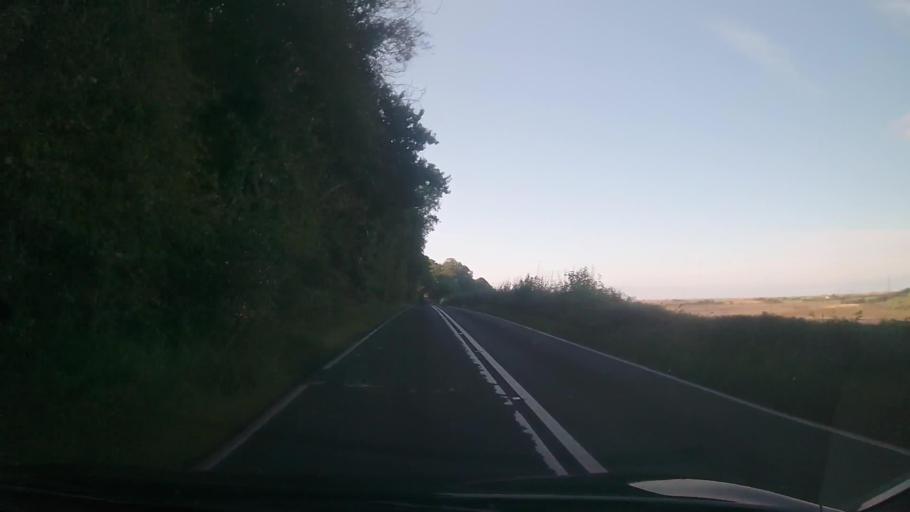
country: GB
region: England
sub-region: Cumbria
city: Seascale
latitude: 54.3641
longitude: -3.3969
